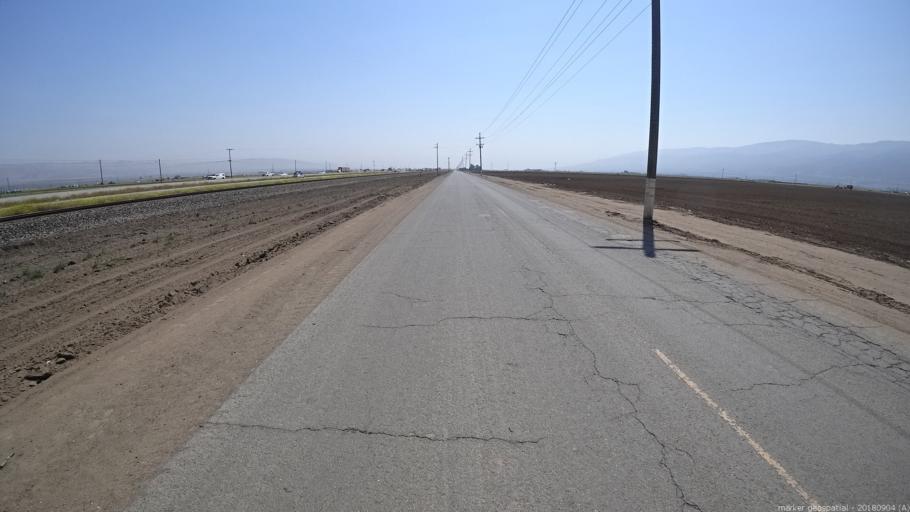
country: US
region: California
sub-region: Monterey County
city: Chualar
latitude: 36.5387
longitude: -121.4850
